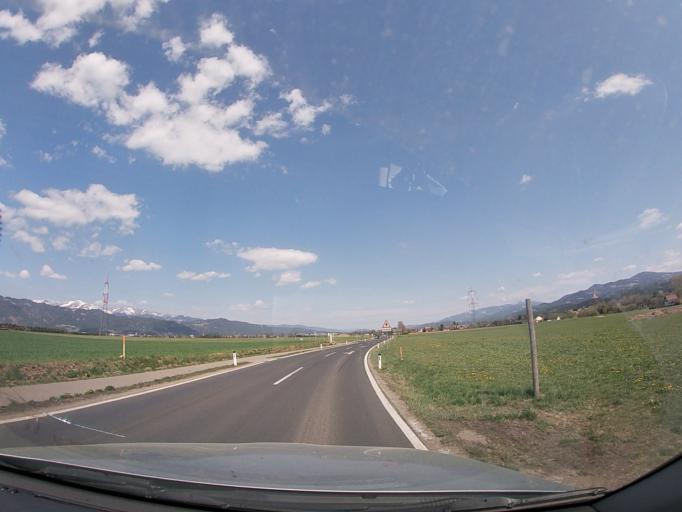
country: AT
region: Styria
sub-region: Politischer Bezirk Murtal
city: Weisskirchen in Steiermark
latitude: 47.1657
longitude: 14.7404
